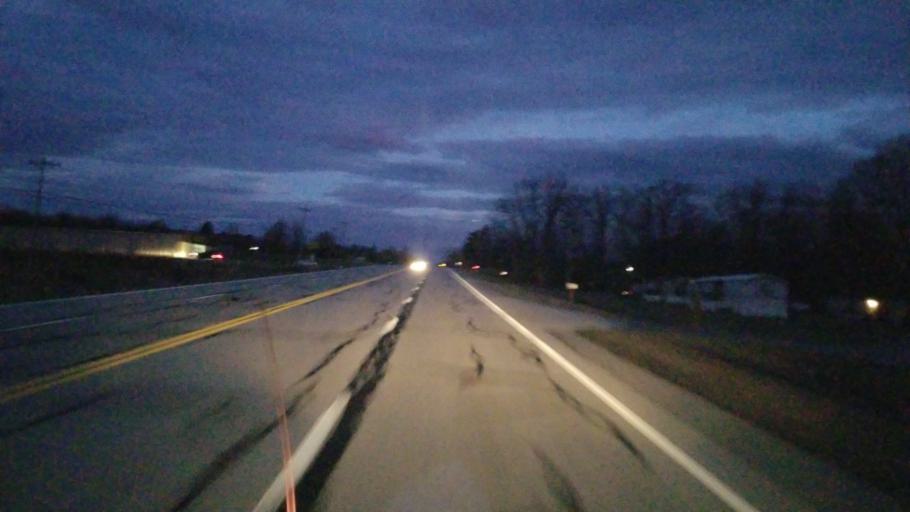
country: US
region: Tennessee
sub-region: Sequatchie County
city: Dunlap
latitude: 35.4783
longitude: -85.4630
